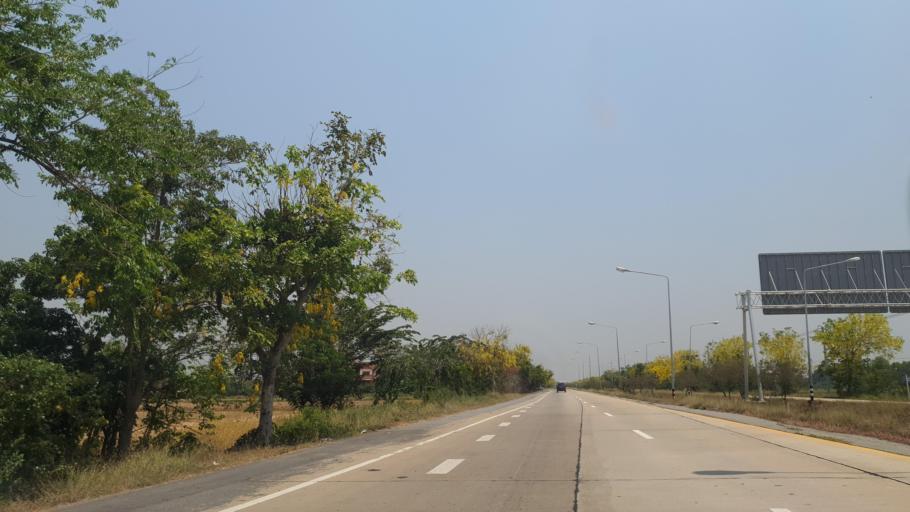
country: TH
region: Suphan Buri
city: Suphan Buri
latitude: 14.5055
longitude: 100.0498
